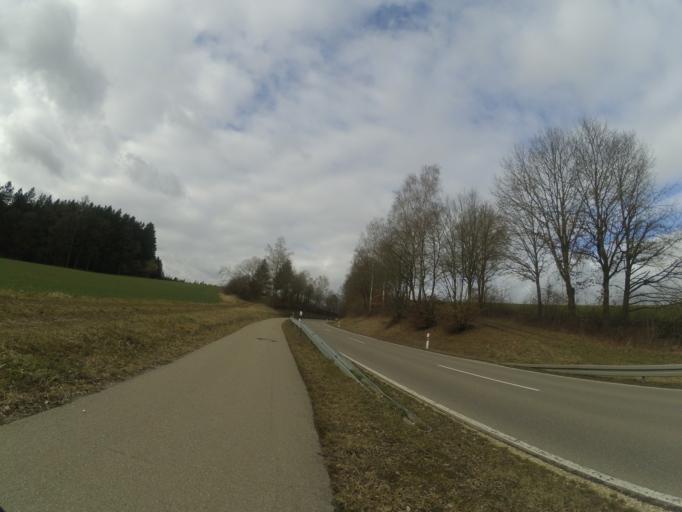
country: DE
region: Bavaria
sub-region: Swabia
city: Bellenberg
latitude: 48.2773
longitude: 10.1214
